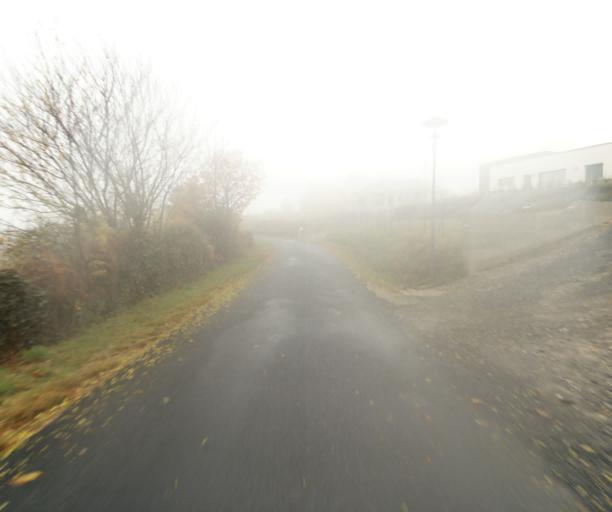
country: FR
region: Limousin
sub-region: Departement de la Correze
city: Sainte-Fereole
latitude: 45.1920
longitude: 1.6285
